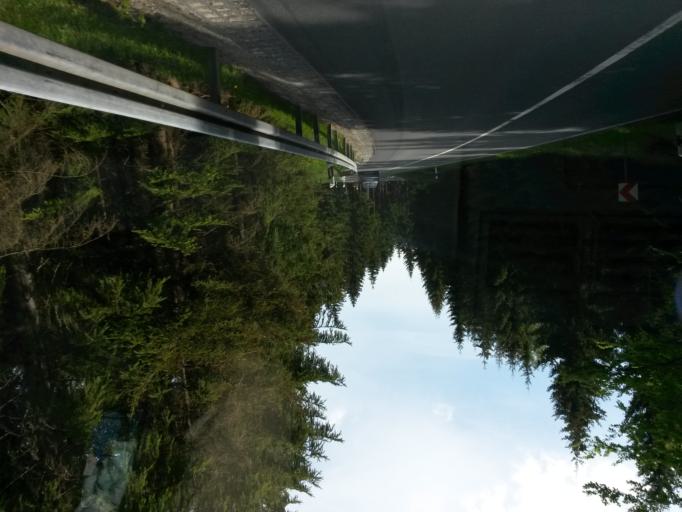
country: DE
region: Saxony
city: Zwota
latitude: 50.3619
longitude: 12.4165
